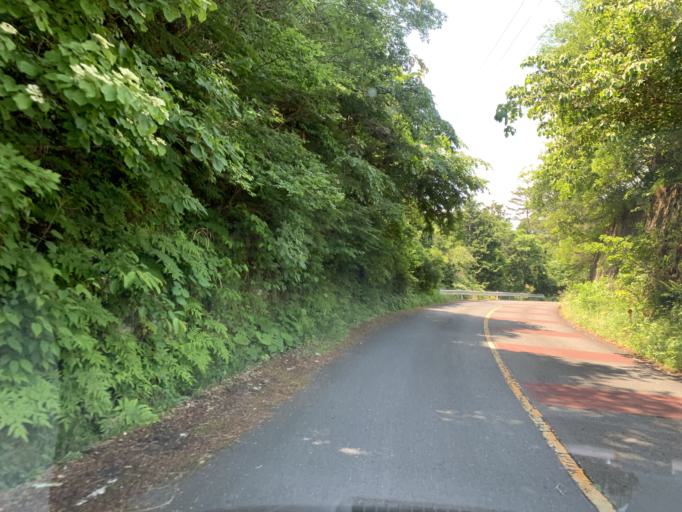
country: JP
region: Miyagi
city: Matsushima
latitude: 38.3603
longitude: 141.0535
